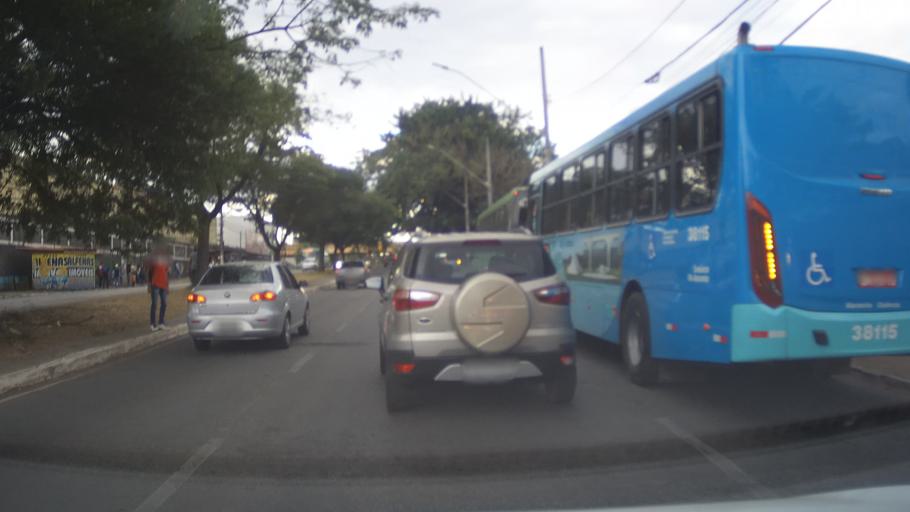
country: BR
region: Minas Gerais
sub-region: Contagem
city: Contagem
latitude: -19.9543
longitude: -44.0176
